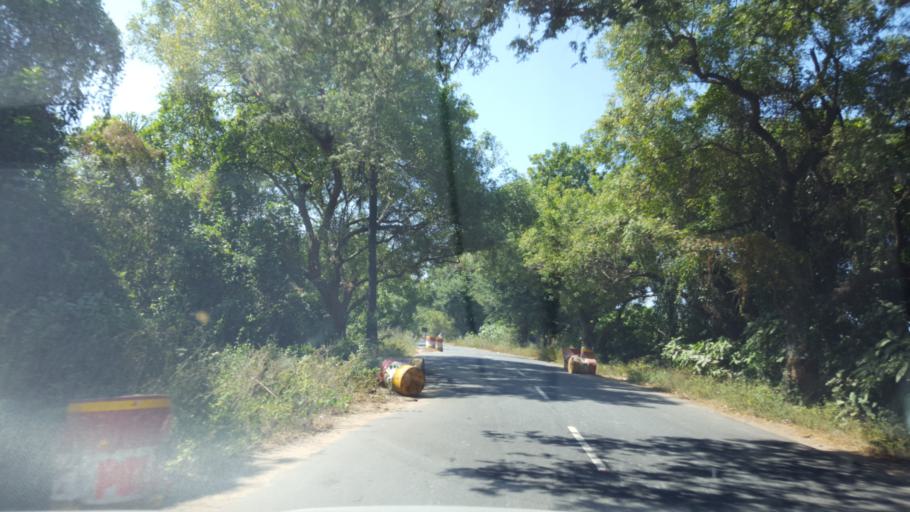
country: IN
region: Tamil Nadu
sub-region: Kancheepuram
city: Chengalpattu
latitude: 12.7515
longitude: 79.9334
